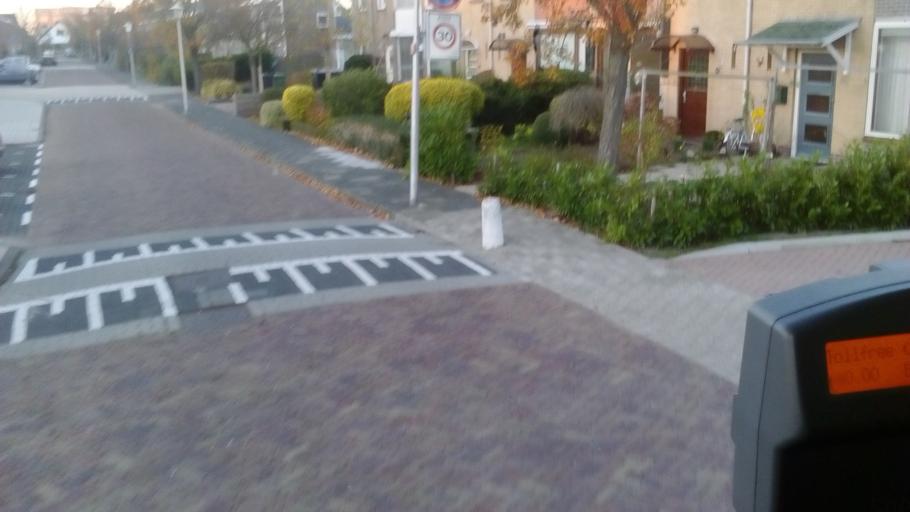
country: NL
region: South Holland
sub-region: Gemeente Westland
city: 's-Gravenzande
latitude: 52.0043
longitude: 4.1738
